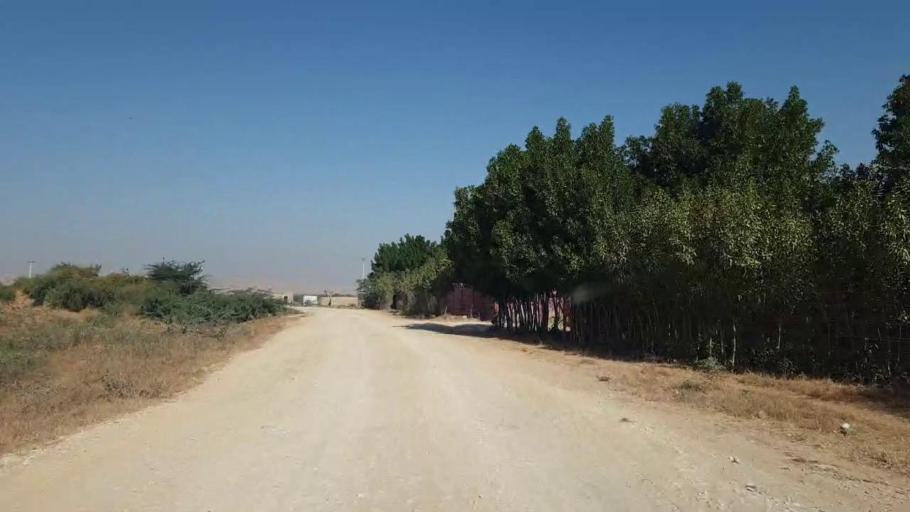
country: PK
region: Sindh
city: Gharo
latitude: 25.1715
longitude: 67.7331
